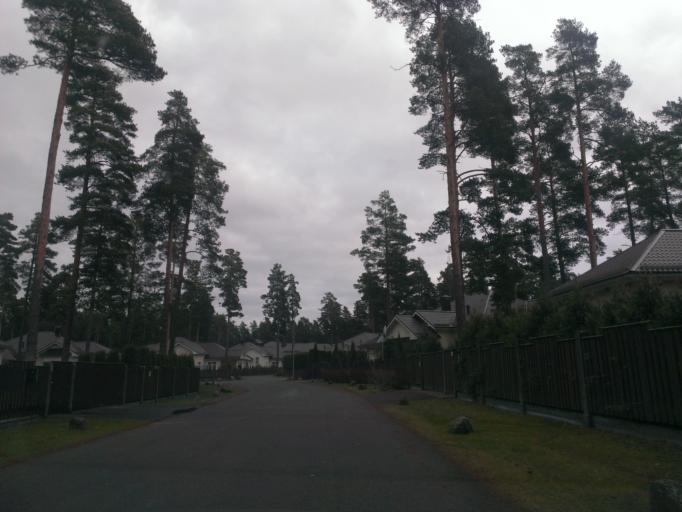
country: LV
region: Riga
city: Bergi
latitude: 56.9956
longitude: 24.3035
